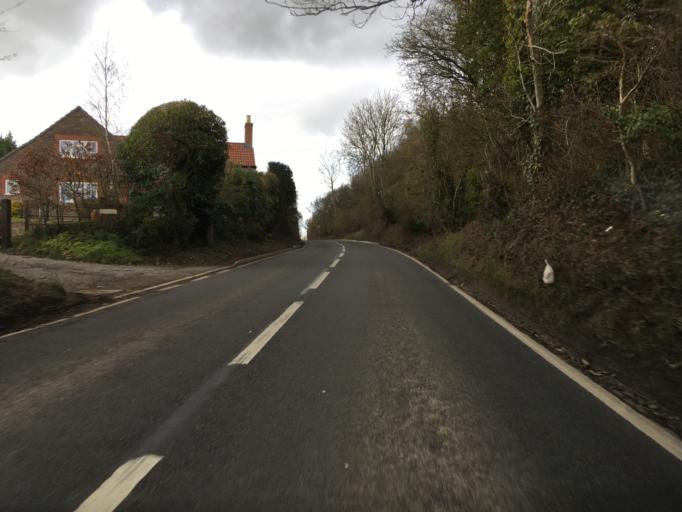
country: GB
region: England
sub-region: South Gloucestershire
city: Tytherington
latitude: 51.5627
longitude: -2.4913
